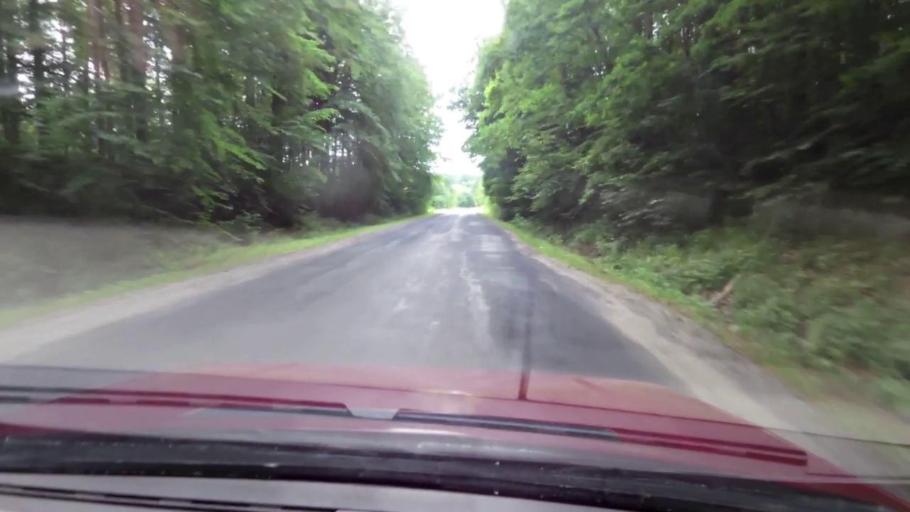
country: PL
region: Pomeranian Voivodeship
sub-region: Powiat slupski
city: Kepice
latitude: 54.2708
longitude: 16.9915
